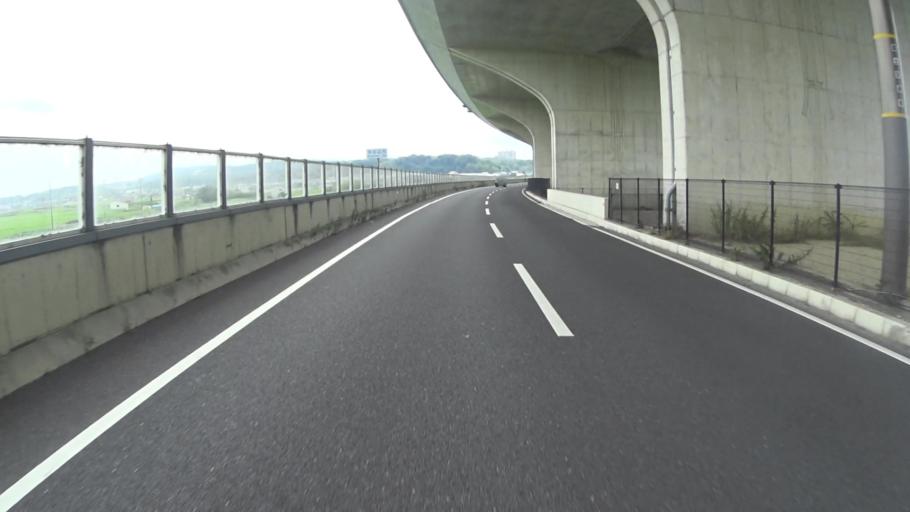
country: JP
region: Kyoto
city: Yawata
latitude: 34.8545
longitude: 135.7341
